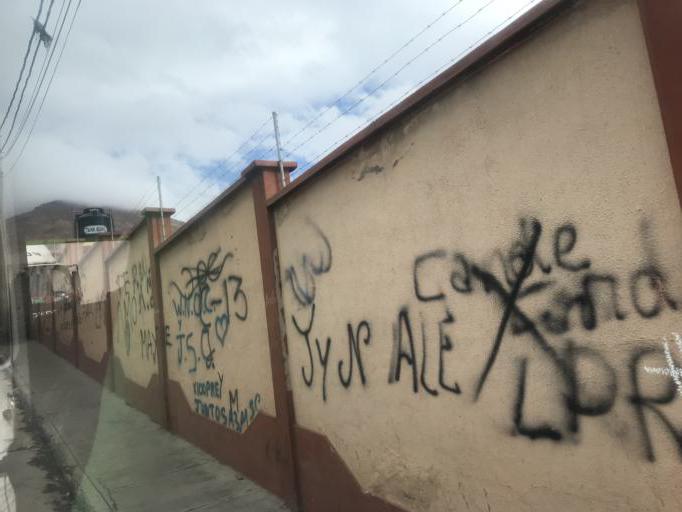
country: BO
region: Potosi
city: Potosi
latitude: -19.6000
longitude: -65.7464
